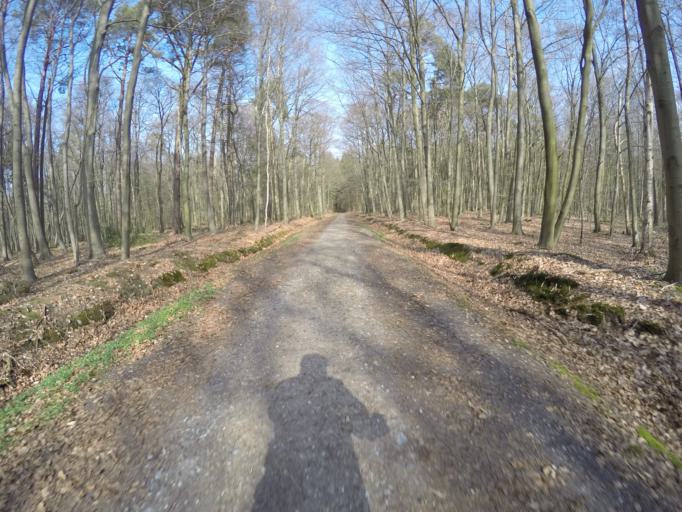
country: DE
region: Schleswig-Holstein
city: Borstel-Hohenraden
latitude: 53.7189
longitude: 9.8186
